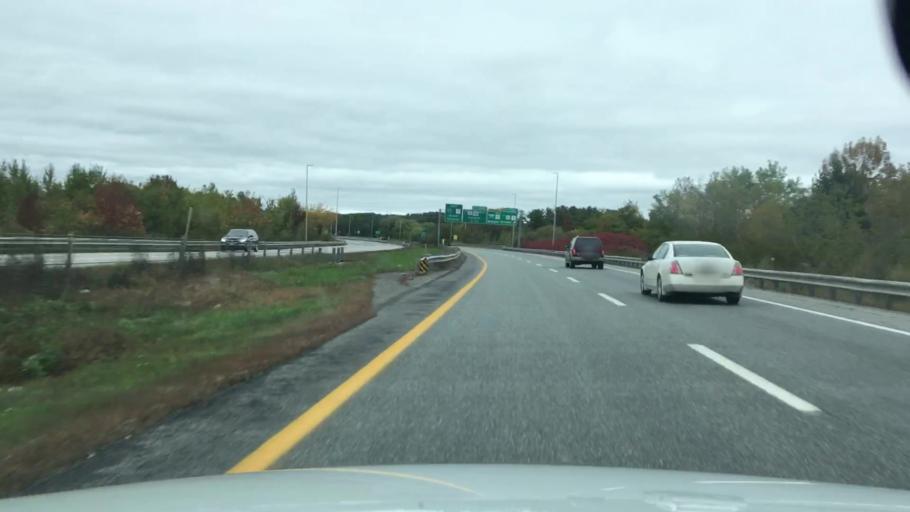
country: US
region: Maine
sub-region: Penobscot County
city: Bangor
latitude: 44.7824
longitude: -68.8130
